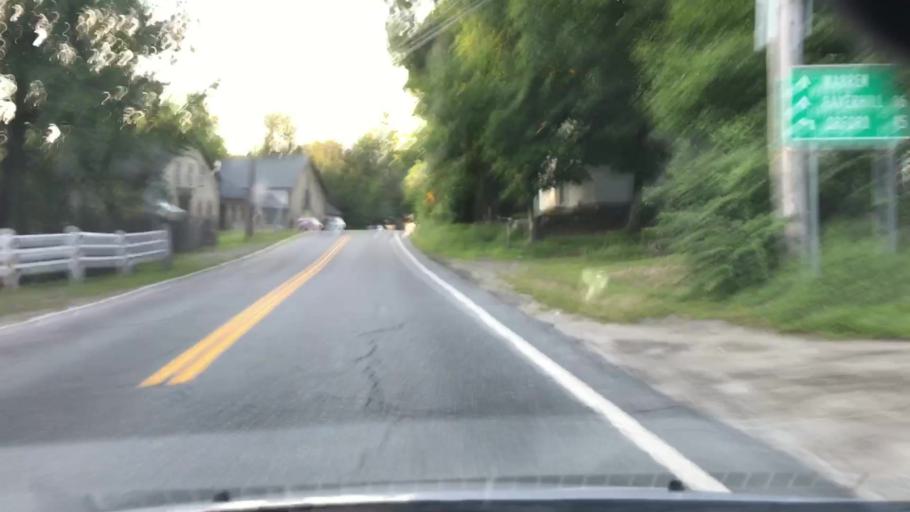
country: US
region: New Hampshire
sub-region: Grafton County
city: Rumney
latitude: 43.8708
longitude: -71.9124
